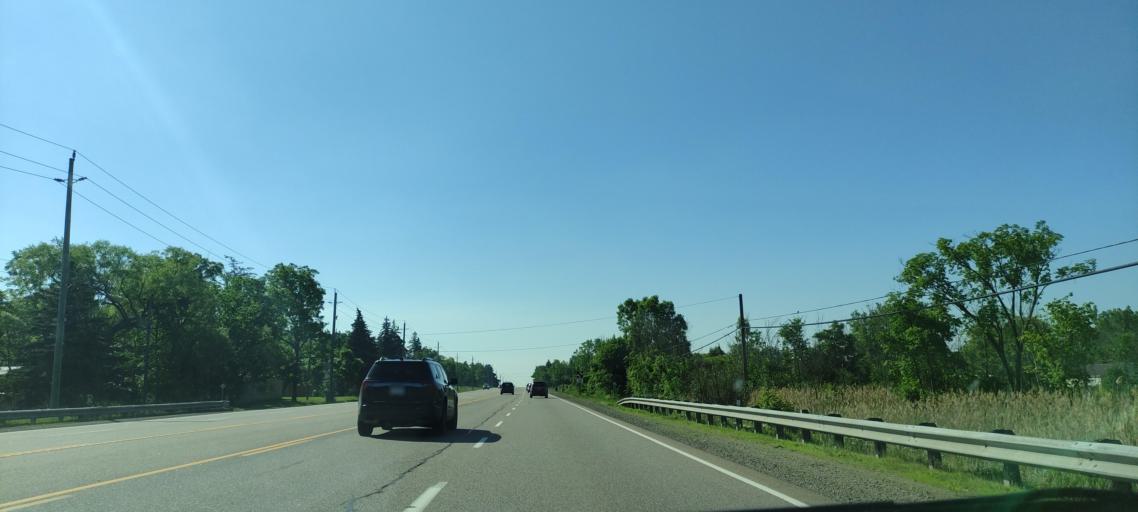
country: CA
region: Ontario
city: Burlington
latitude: 43.3269
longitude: -79.9381
